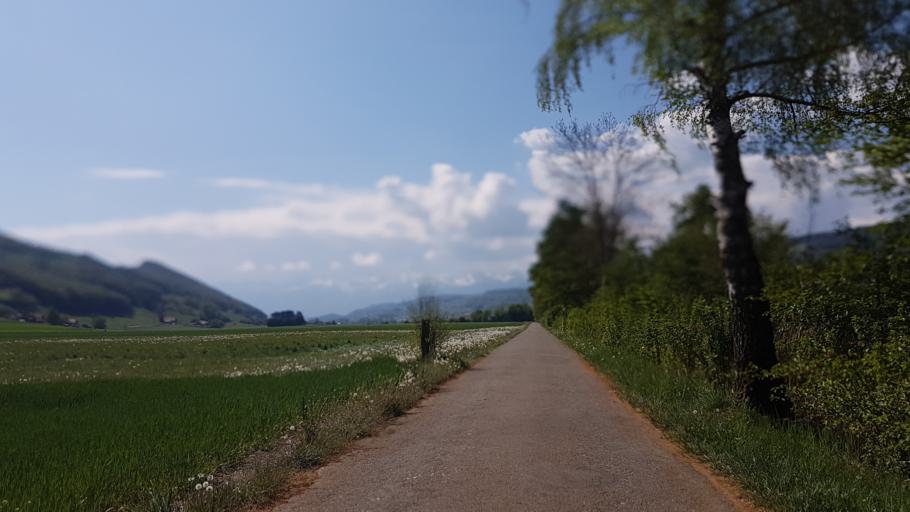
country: CH
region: Bern
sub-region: Bern-Mittelland District
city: Belp
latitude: 46.8776
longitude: 7.4998
